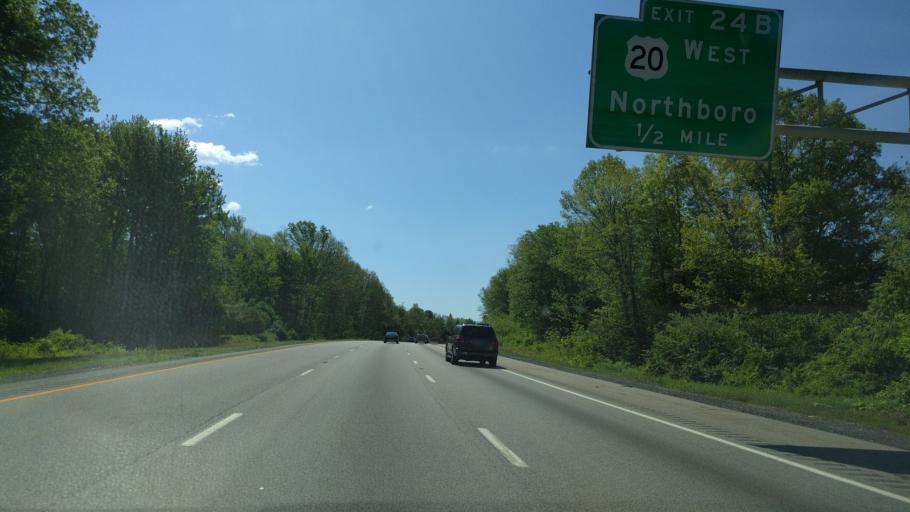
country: US
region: Massachusetts
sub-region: Middlesex County
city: Marlborough
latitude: 42.3511
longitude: -71.5783
